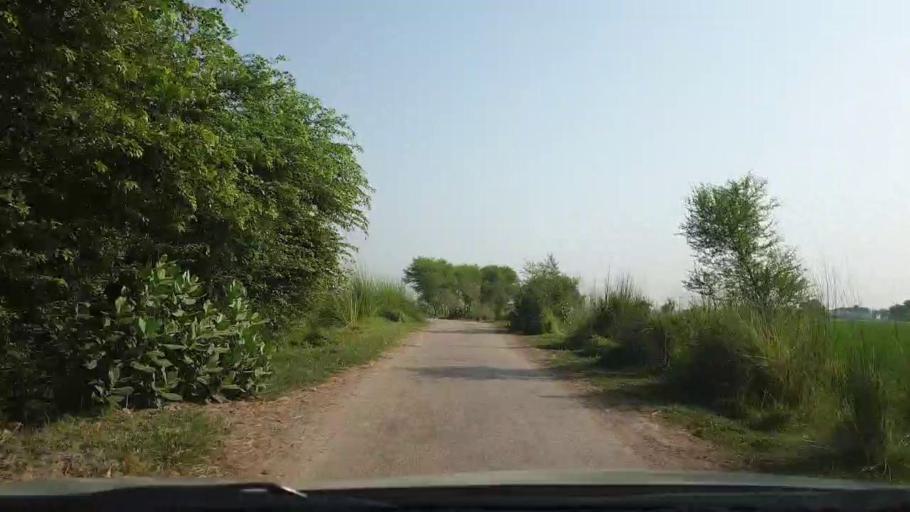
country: PK
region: Sindh
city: Goth Garelo
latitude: 27.4736
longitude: 68.1186
